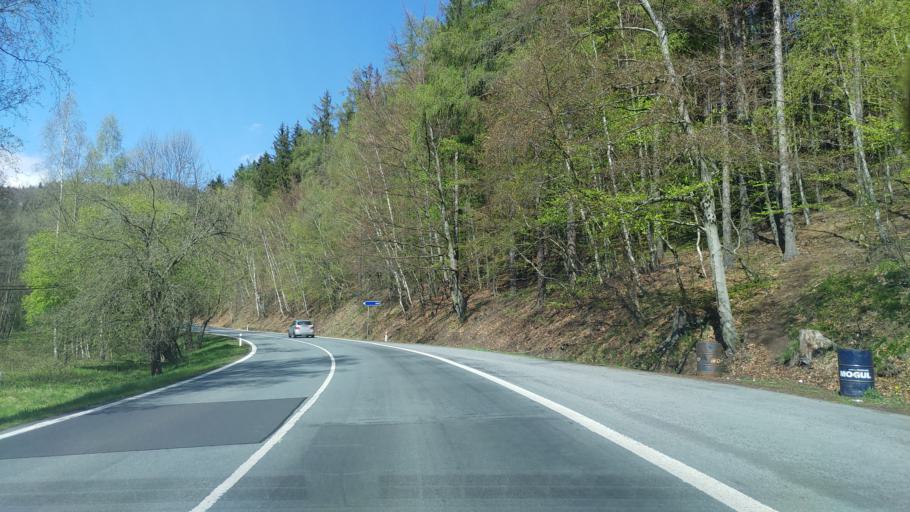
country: CZ
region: Ustecky
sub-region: Okres Chomutov
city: Perstejn
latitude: 50.3684
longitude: 13.0875
